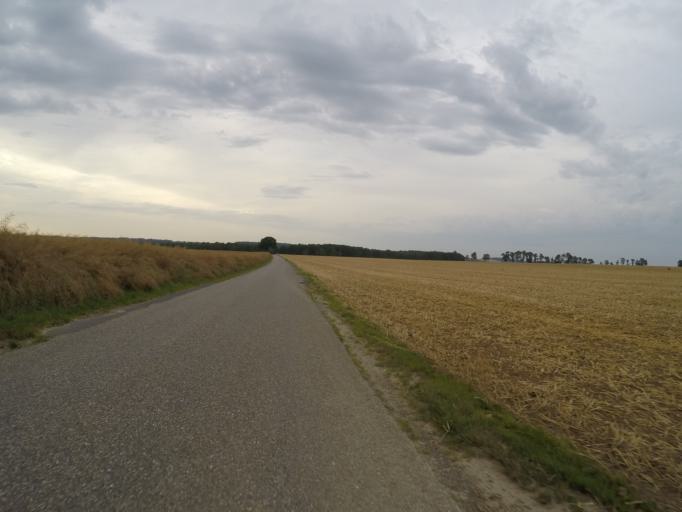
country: BE
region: Wallonia
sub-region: Province de Namur
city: Assesse
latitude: 50.3093
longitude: 5.0367
